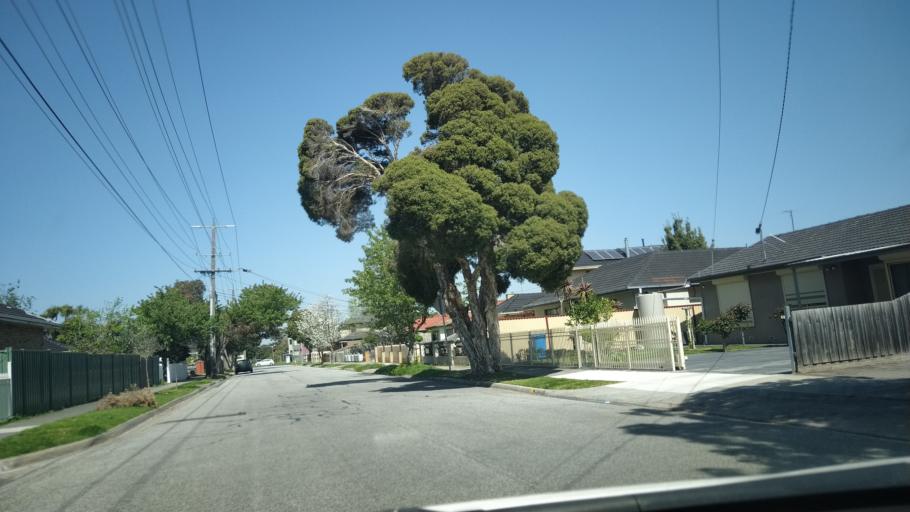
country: AU
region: Victoria
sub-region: Greater Dandenong
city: Noble Park
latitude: -37.9710
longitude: 145.1605
